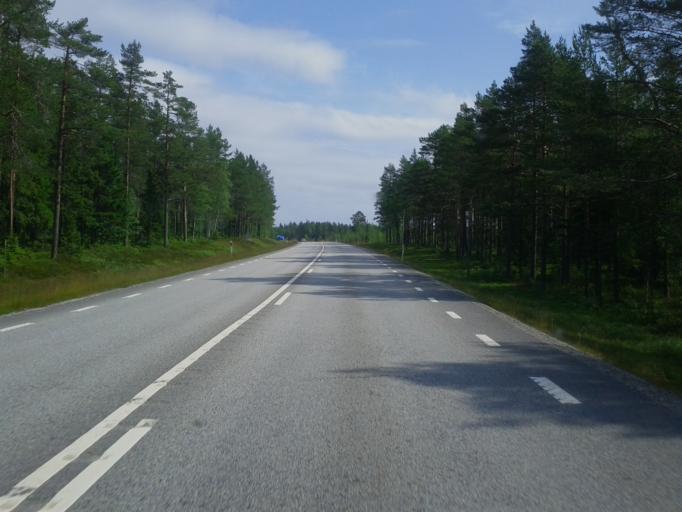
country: SE
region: Vaesterbotten
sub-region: Robertsfors Kommun
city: Robertsfors
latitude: 64.1838
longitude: 20.9884
